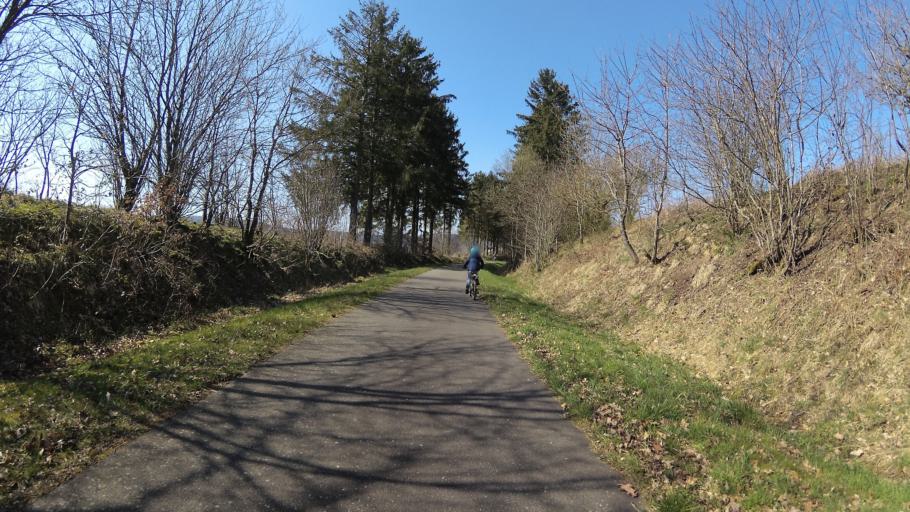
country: DE
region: Rheinland-Pfalz
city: Reinsfeld
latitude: 49.6740
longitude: 6.8913
